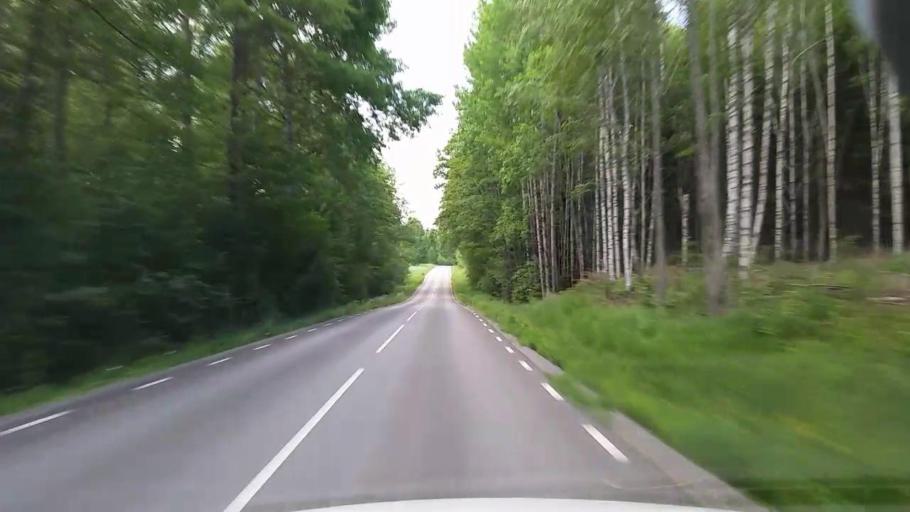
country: SE
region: Vaestmanland
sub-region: Kopings Kommun
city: Kolsva
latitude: 59.7565
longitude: 15.8342
